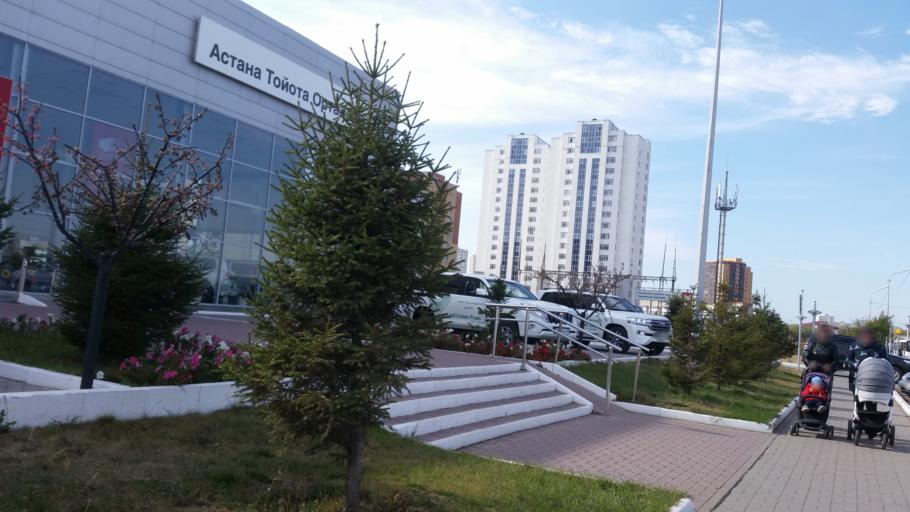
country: KZ
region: Astana Qalasy
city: Astana
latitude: 51.1633
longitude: 71.4809
